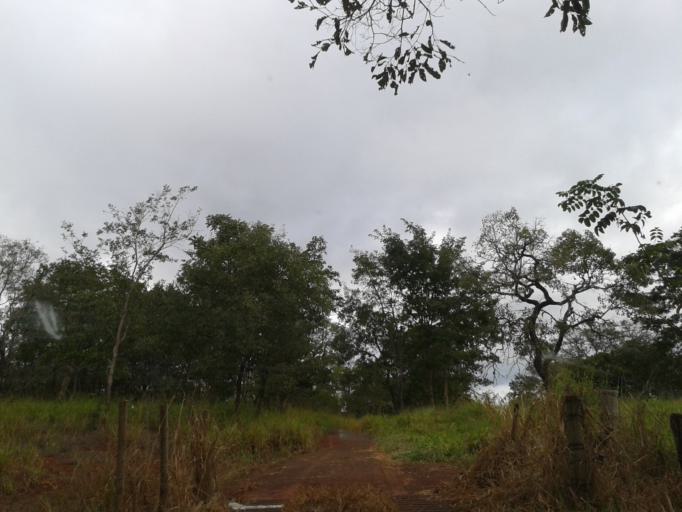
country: BR
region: Minas Gerais
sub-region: Campina Verde
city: Campina Verde
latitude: -19.4863
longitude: -49.6227
